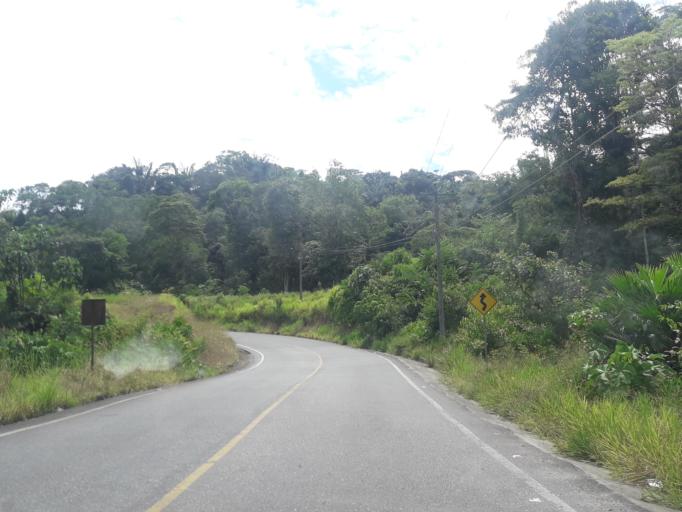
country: EC
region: Napo
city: Tena
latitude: -1.0160
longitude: -77.8606
